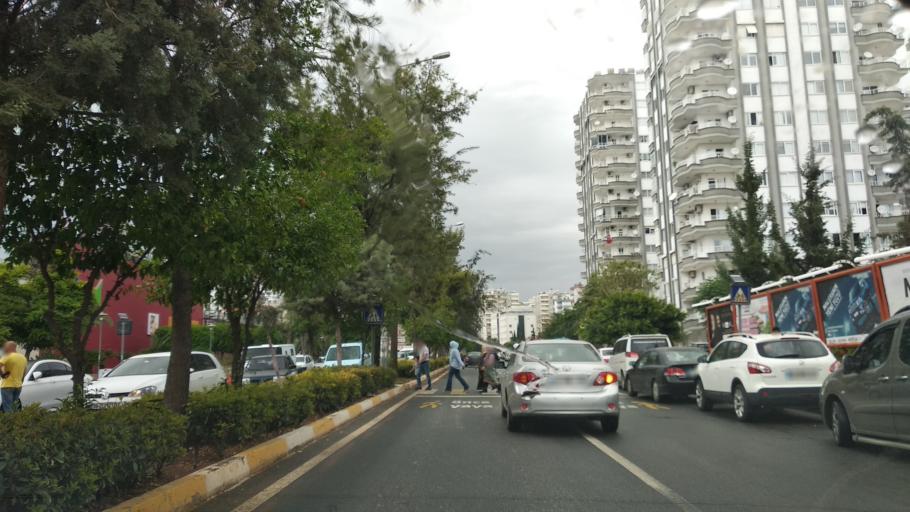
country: TR
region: Mersin
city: Mercin
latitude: 36.7860
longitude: 34.5889
